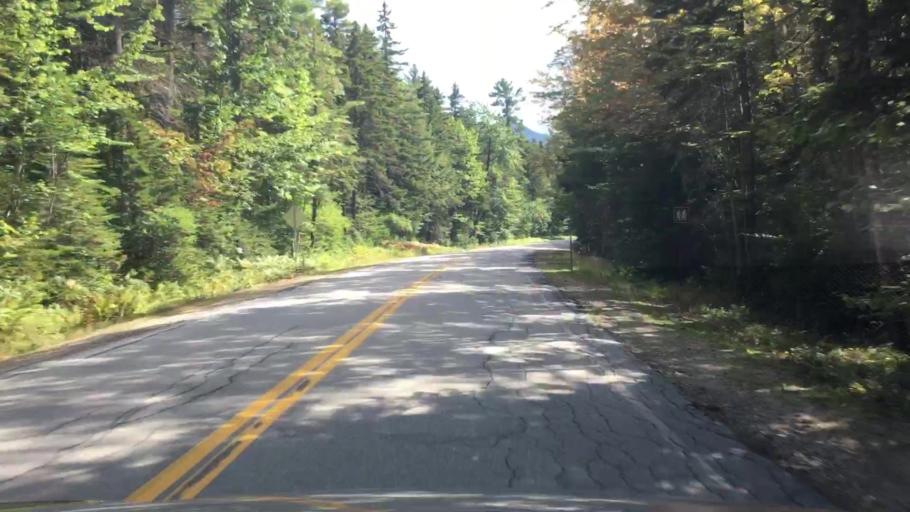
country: US
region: New Hampshire
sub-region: Carroll County
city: Tamworth
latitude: 44.0039
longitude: -71.3206
